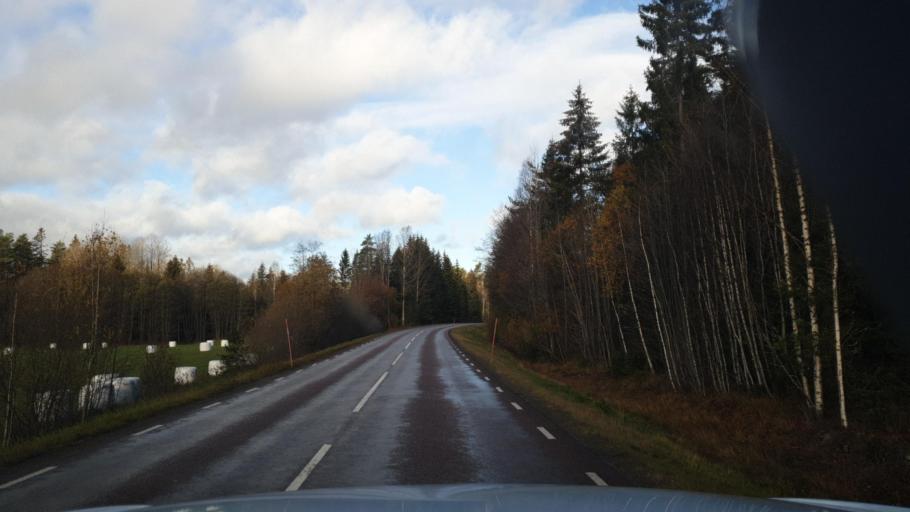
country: SE
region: Vaermland
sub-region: Grums Kommun
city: Slottsbron
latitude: 59.4184
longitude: 12.9835
